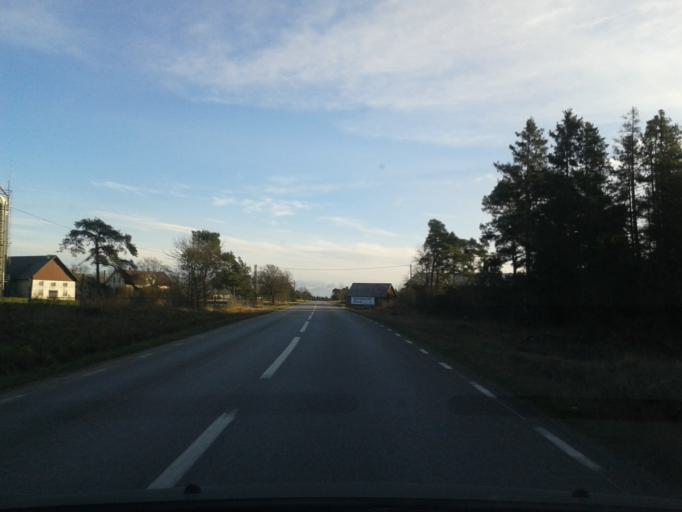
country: SE
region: Gotland
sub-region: Gotland
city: Hemse
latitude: 57.3670
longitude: 18.6701
